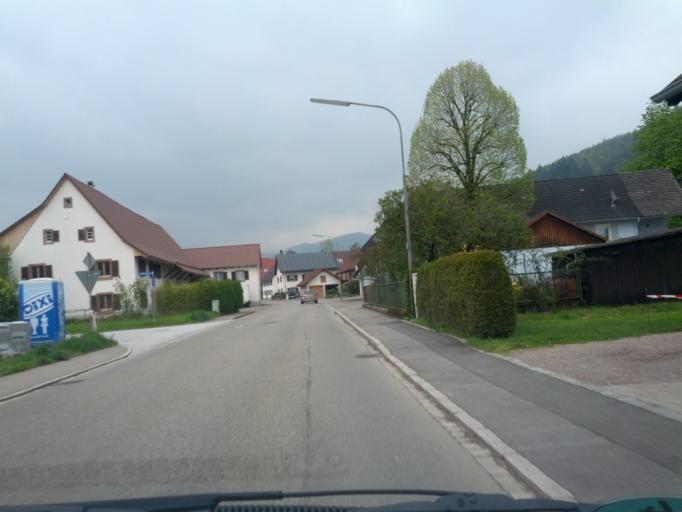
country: DE
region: Baden-Wuerttemberg
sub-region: Freiburg Region
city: Schopfheim
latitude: 47.6618
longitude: 7.8002
